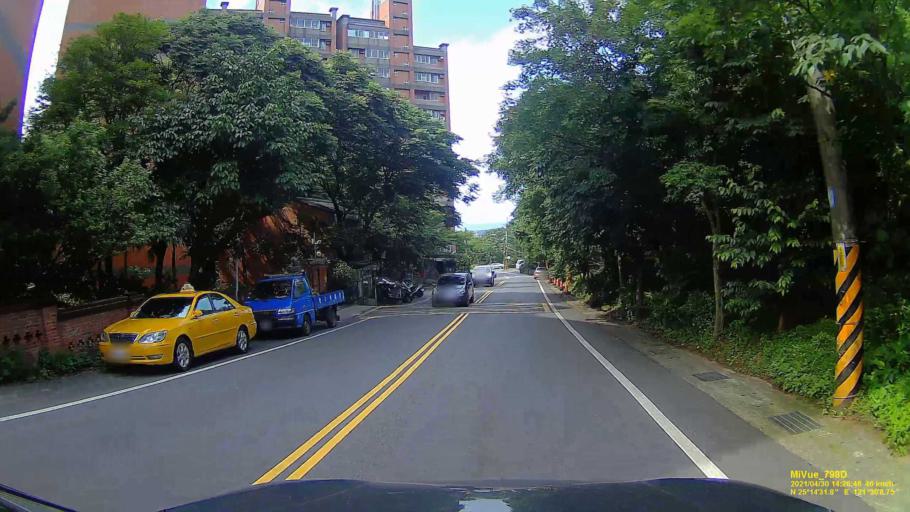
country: TW
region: Taipei
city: Taipei
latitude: 25.2425
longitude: 121.5025
